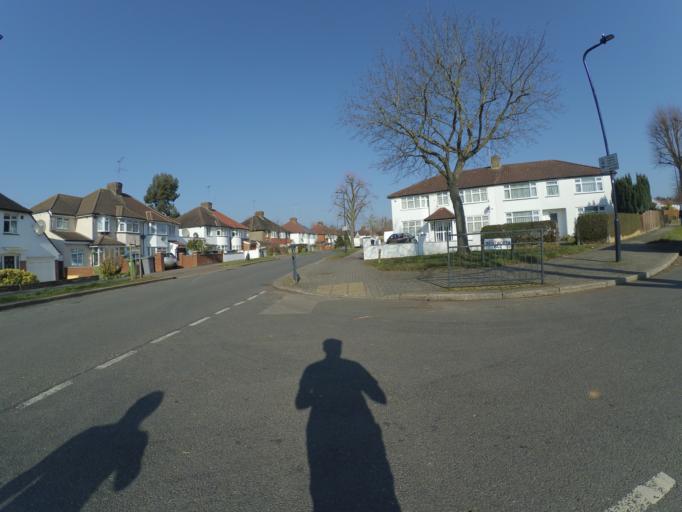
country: GB
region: England
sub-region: Greater London
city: Wembley
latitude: 51.5734
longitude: -0.2890
